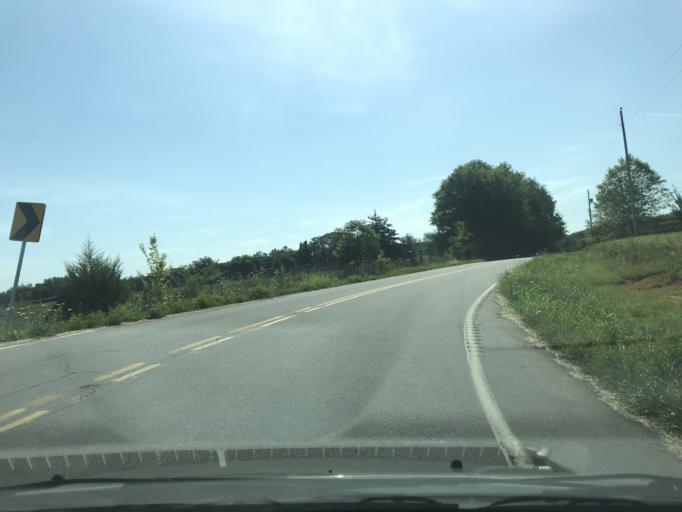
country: US
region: Tennessee
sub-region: Hamilton County
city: Sale Creek
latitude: 35.2935
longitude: -85.0462
